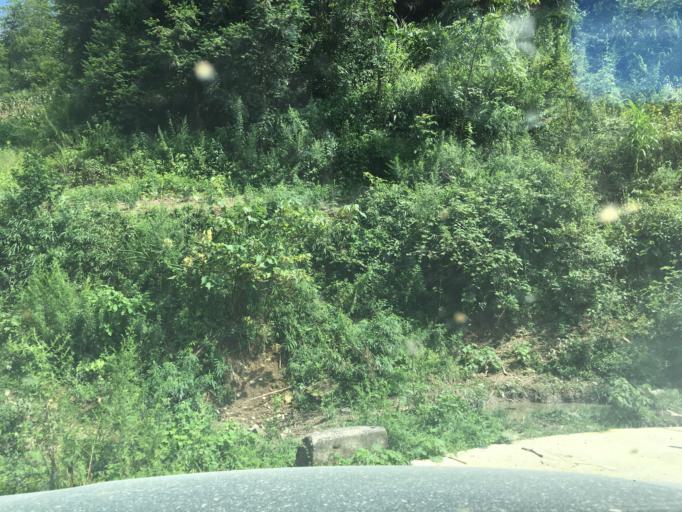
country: CN
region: Guangxi Zhuangzu Zizhiqu
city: Xinzhou
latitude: 24.9694
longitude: 105.6189
